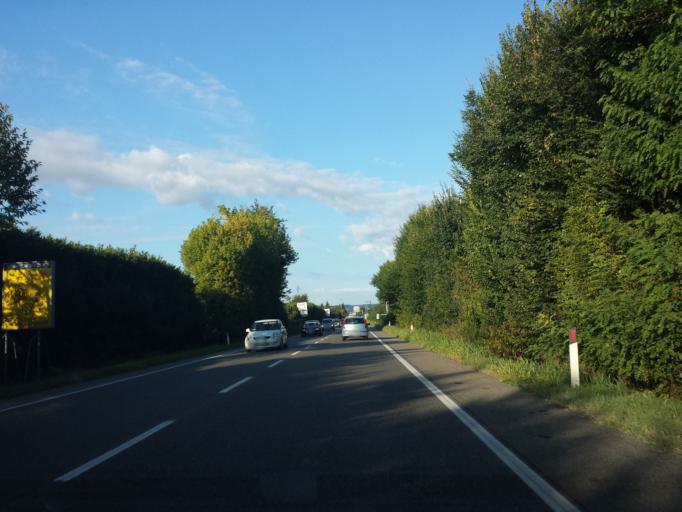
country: IT
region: Veneto
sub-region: Provincia di Vicenza
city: Altavilla Vicentina
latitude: 45.5148
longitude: 11.4644
